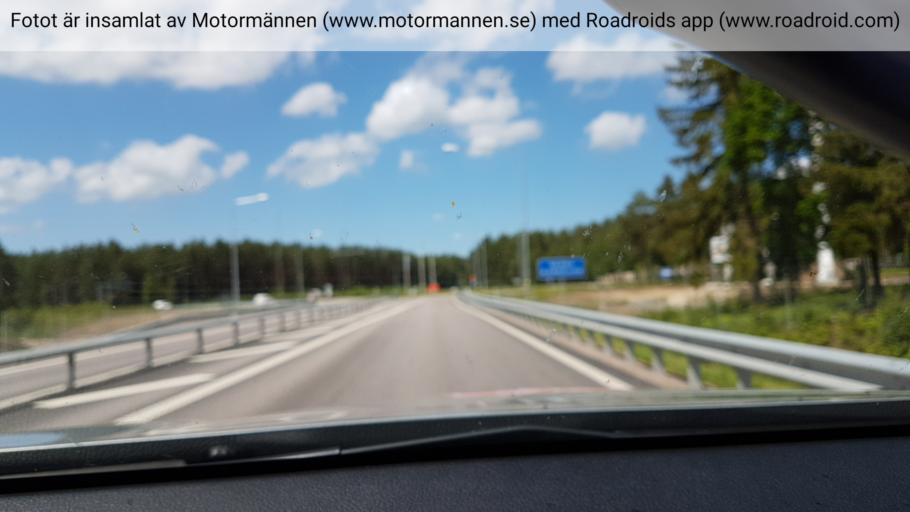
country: SE
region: Vaestra Goetaland
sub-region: Lidkopings Kommun
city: Lidkoping
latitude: 58.4875
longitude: 13.1886
